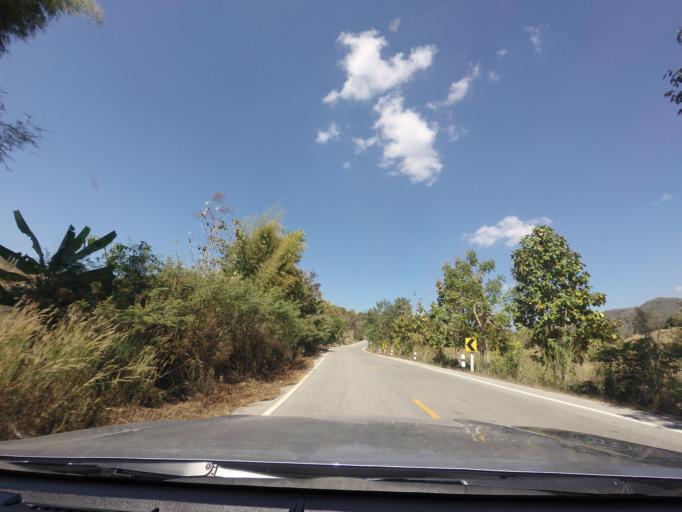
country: TH
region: Lampang
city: Chae Hom
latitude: 18.5679
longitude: 99.6248
